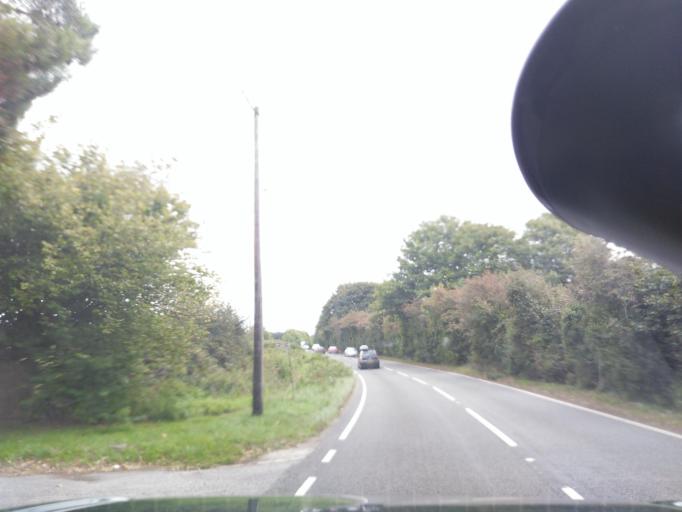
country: GB
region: England
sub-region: Dorset
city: Lytchett Matravers
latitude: 50.7395
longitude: -2.1054
